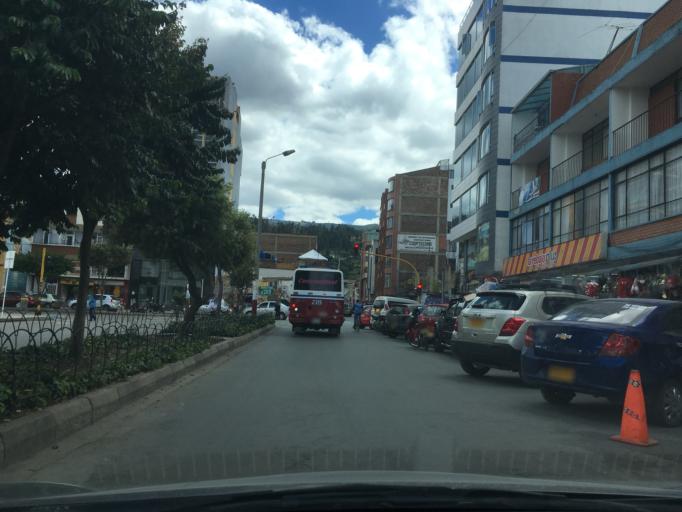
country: CO
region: Boyaca
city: Sogamoso
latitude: 5.7187
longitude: -72.9267
